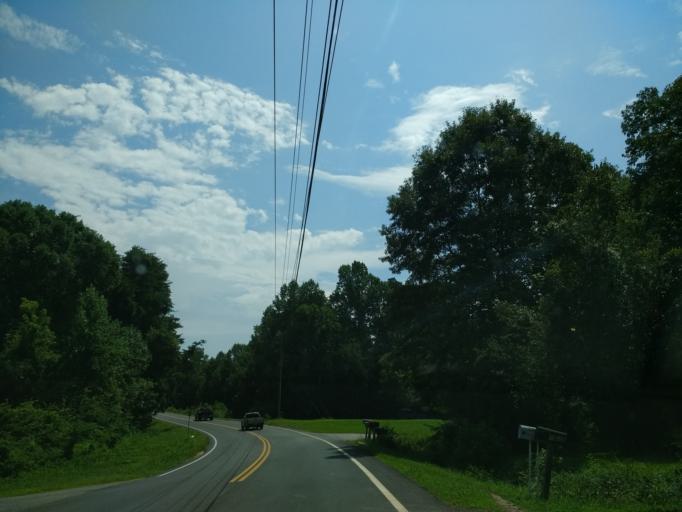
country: US
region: Georgia
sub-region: White County
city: Cleveland
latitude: 34.6354
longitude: -83.7974
